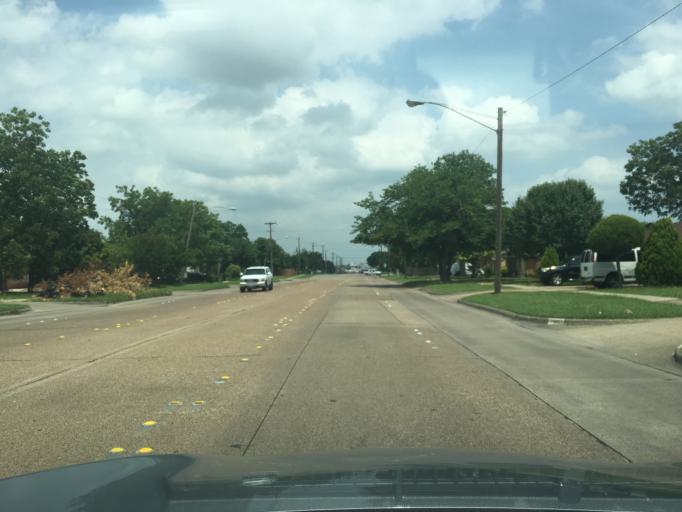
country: US
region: Texas
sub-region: Dallas County
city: Richardson
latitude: 32.9168
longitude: -96.6941
